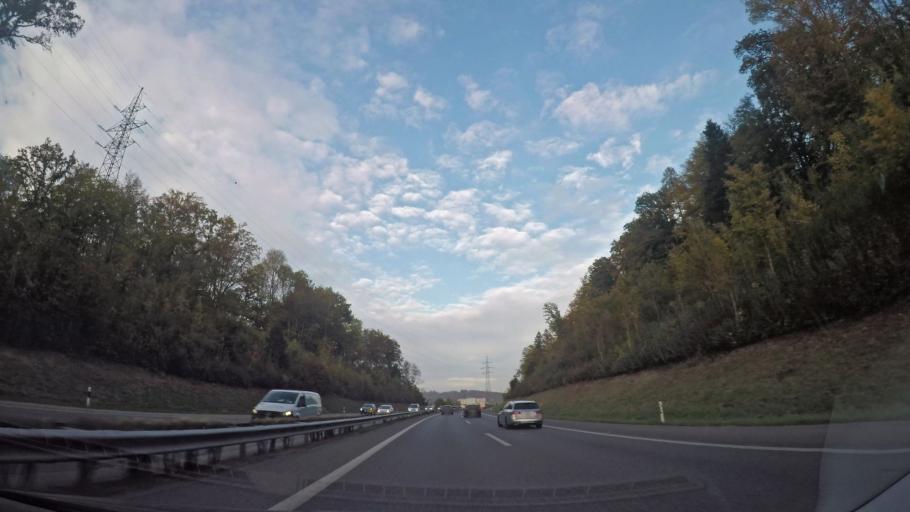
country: CH
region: Aargau
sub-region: Bezirk Aarau
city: Suhr
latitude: 47.3623
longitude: 8.0702
